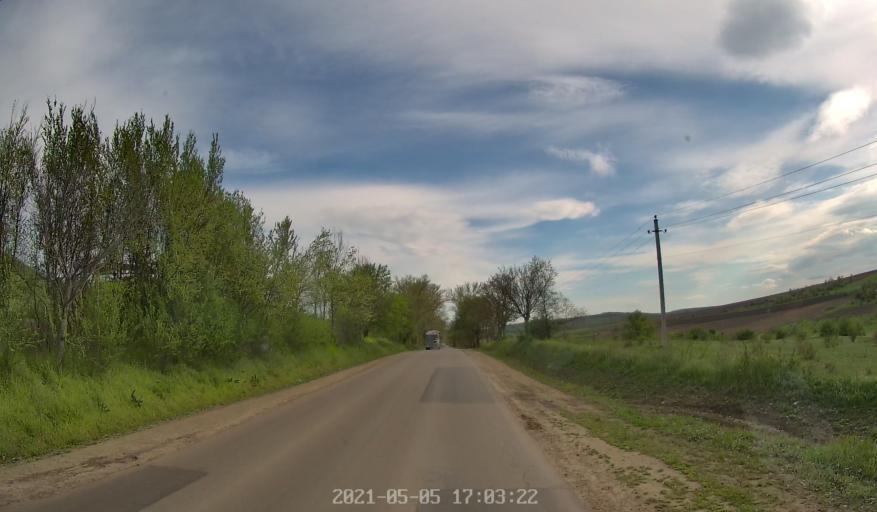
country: MD
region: Chisinau
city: Vadul lui Voda
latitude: 47.0520
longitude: 29.1332
